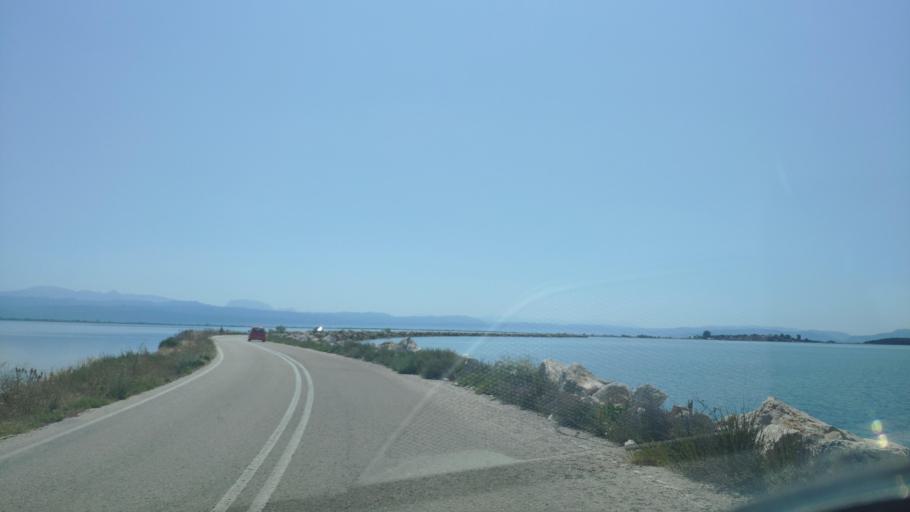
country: GR
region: Epirus
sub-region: Nomos Artas
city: Aneza
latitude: 39.0322
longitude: 20.8938
